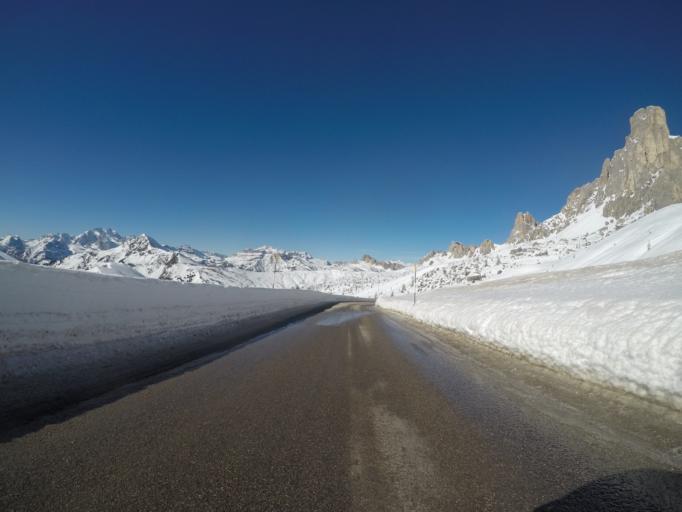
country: IT
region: Veneto
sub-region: Provincia di Belluno
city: Selva di Cadore
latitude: 46.4834
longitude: 12.0527
